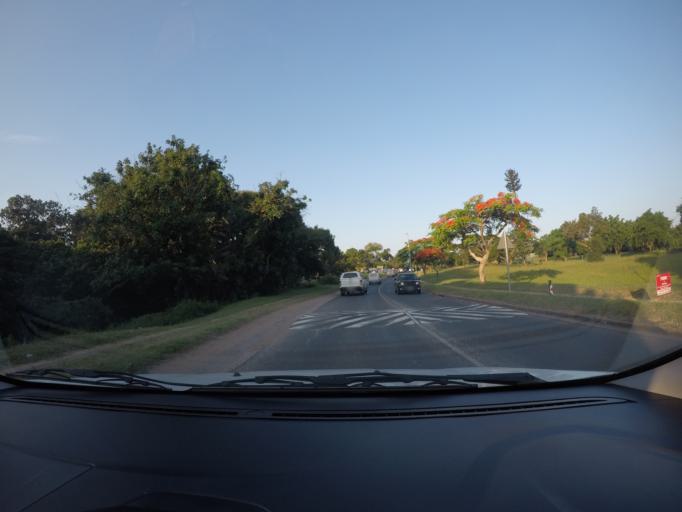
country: ZA
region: KwaZulu-Natal
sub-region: uThungulu District Municipality
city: Richards Bay
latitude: -28.7788
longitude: 32.1000
